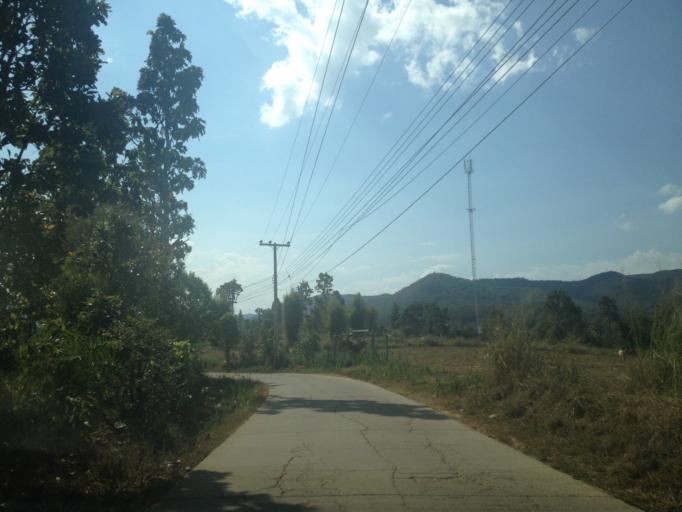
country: TH
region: Mae Hong Son
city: Ban Huai I Huak
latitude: 18.1047
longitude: 98.2182
